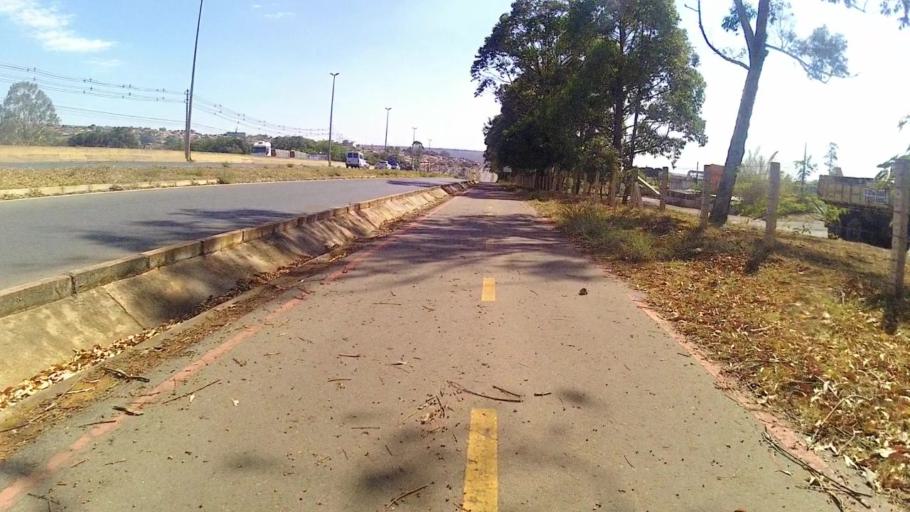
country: BR
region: Federal District
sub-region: Brasilia
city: Brasilia
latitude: -15.6822
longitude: -47.8515
